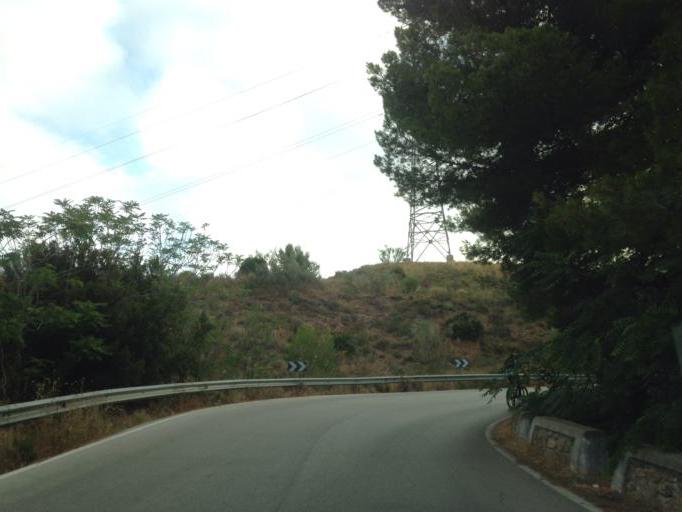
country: ES
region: Andalusia
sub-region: Provincia de Malaga
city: Malaga
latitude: 36.7635
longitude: -4.4069
